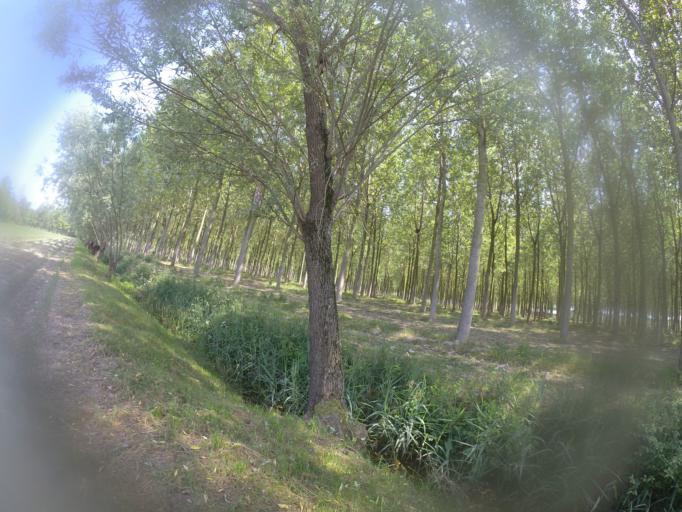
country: IT
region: Friuli Venezia Giulia
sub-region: Provincia di Udine
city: Bertiolo
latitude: 45.9248
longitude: 13.0258
